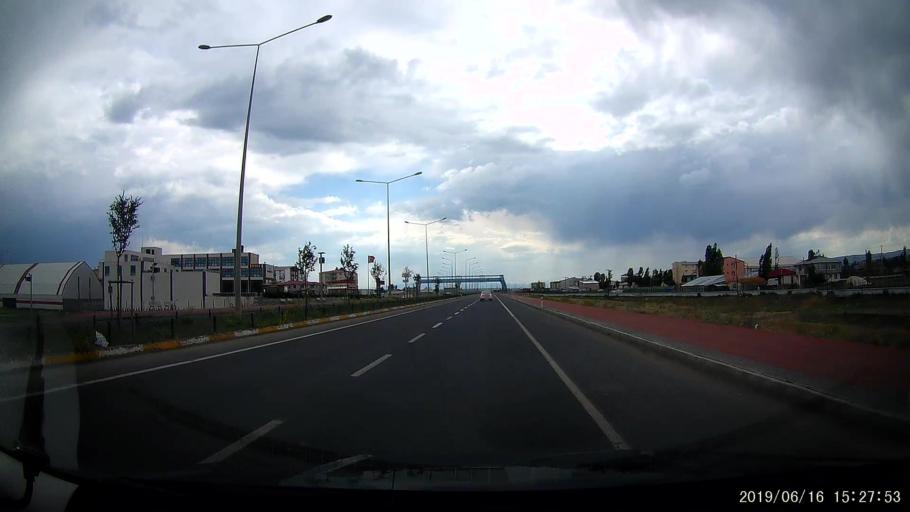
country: TR
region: Erzurum
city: Horasan
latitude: 40.0329
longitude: 42.1506
